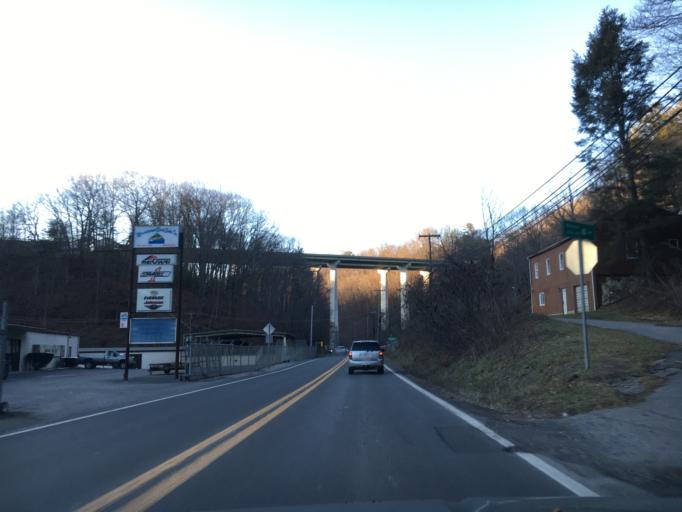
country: US
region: West Virginia
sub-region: Raleigh County
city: Beaver
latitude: 37.7532
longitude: -81.1485
